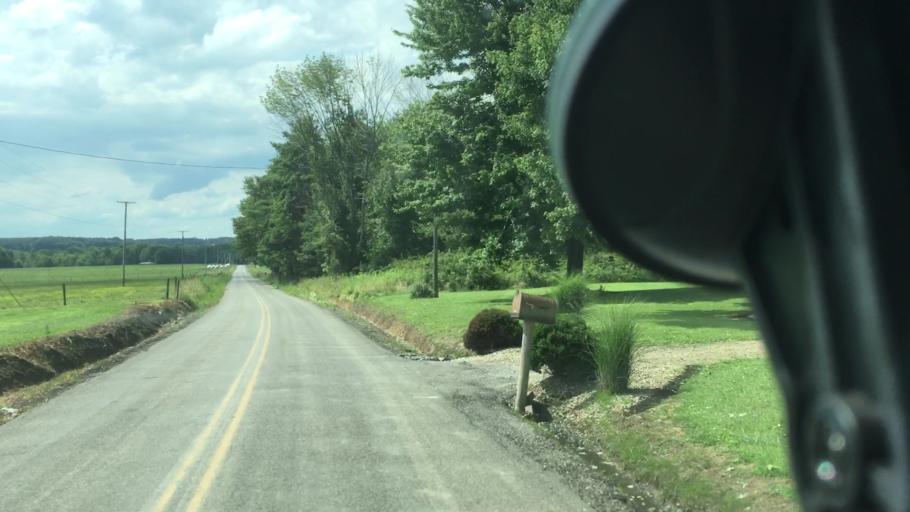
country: US
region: Pennsylvania
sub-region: Mercer County
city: Reynolds Heights
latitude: 41.3036
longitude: -80.3698
